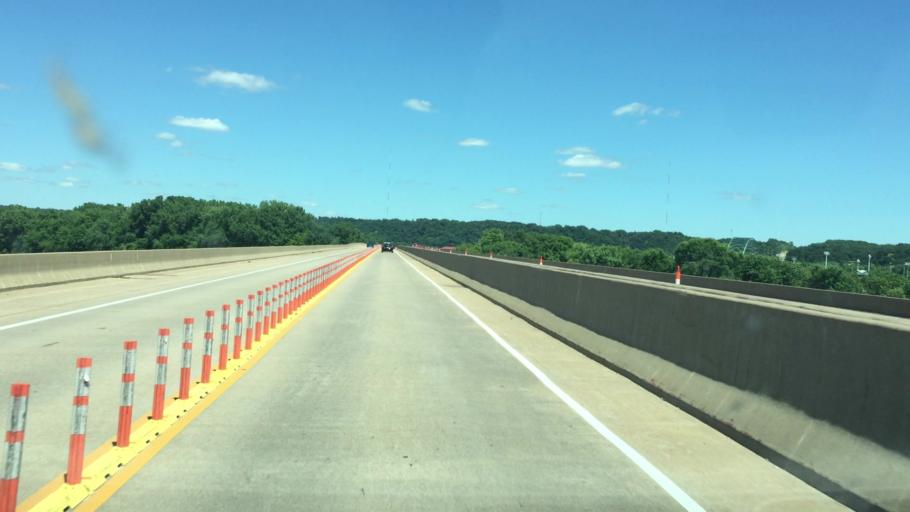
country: US
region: Iowa
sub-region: Dubuque County
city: Dubuque
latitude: 42.5153
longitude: -90.6540
